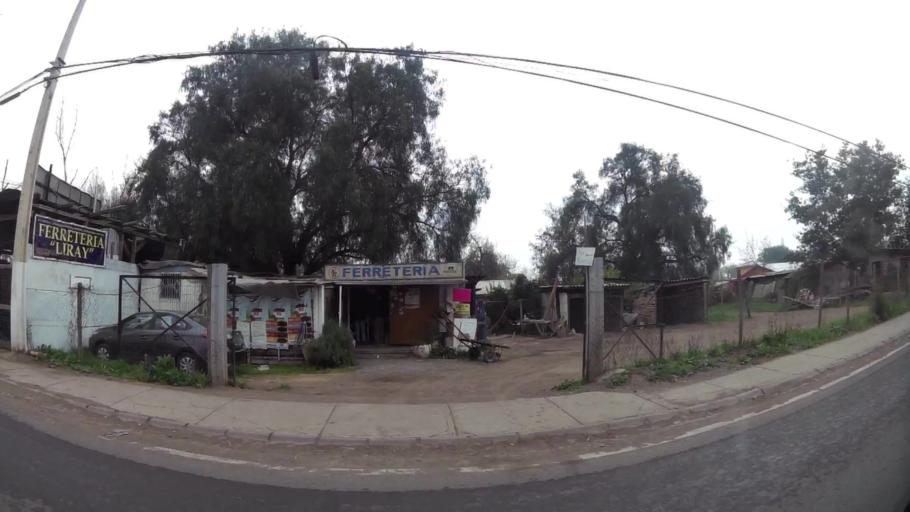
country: CL
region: Santiago Metropolitan
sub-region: Provincia de Chacabuco
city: Chicureo Abajo
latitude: -33.2418
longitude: -70.7352
